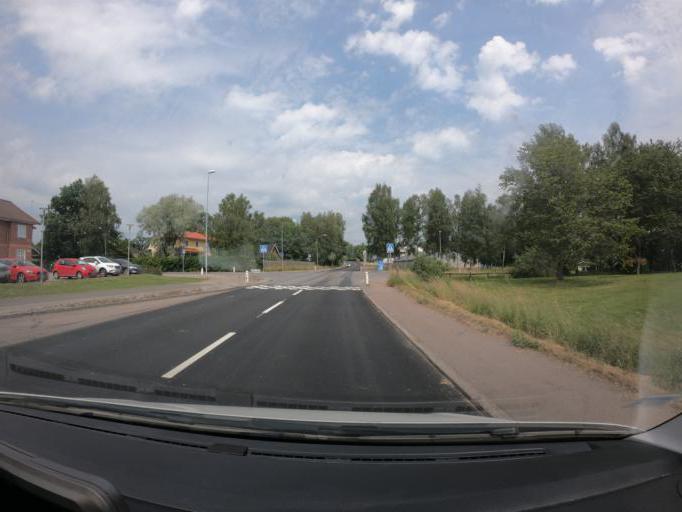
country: SE
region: Skane
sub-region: Hassleholms Kommun
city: Bjarnum
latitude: 56.2833
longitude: 13.7132
